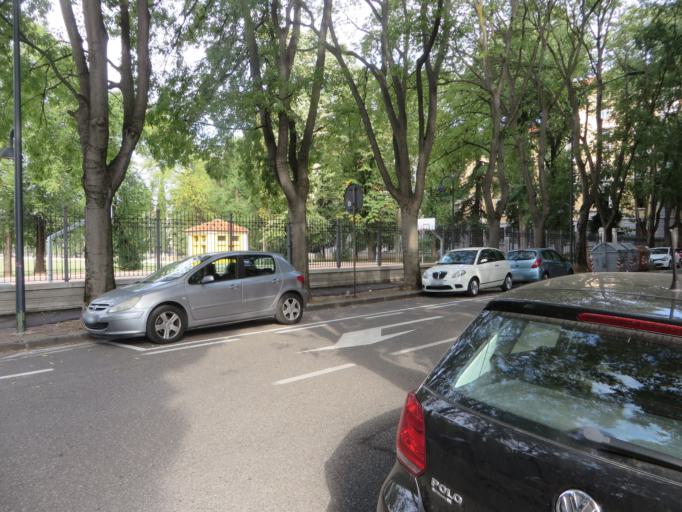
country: IT
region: Lombardy
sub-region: Provincia di Brescia
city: Brescia
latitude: 45.5476
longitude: 10.2184
